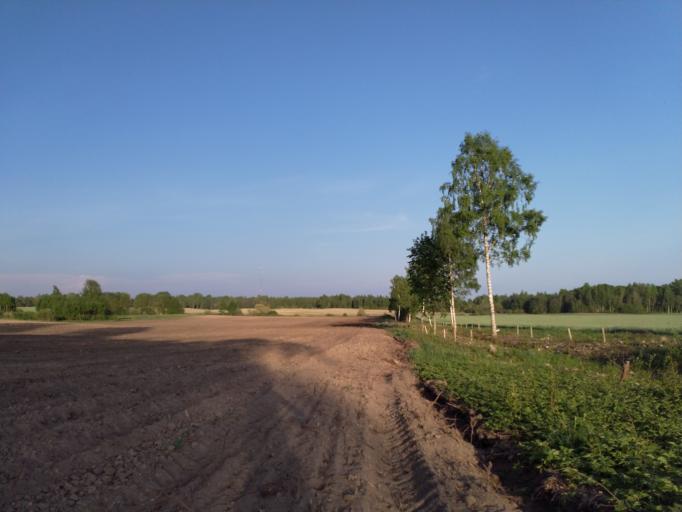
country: LV
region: Aizpute
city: Aizpute
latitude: 56.8294
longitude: 21.7821
